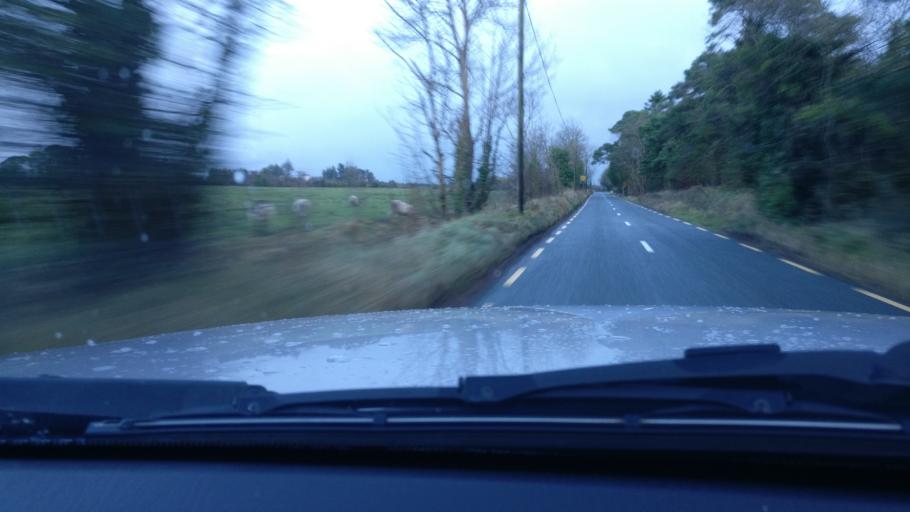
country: IE
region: Connaught
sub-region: County Galway
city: Loughrea
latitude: 53.2236
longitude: -8.3855
